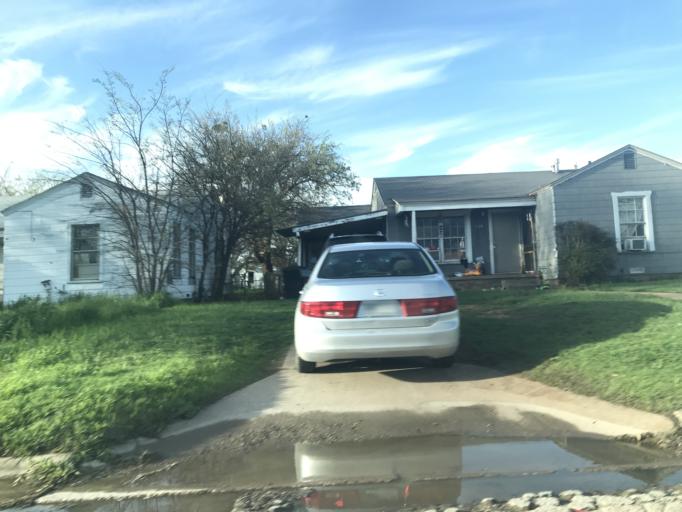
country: US
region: Texas
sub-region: Taylor County
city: Abilene
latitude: 32.4341
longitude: -99.7604
